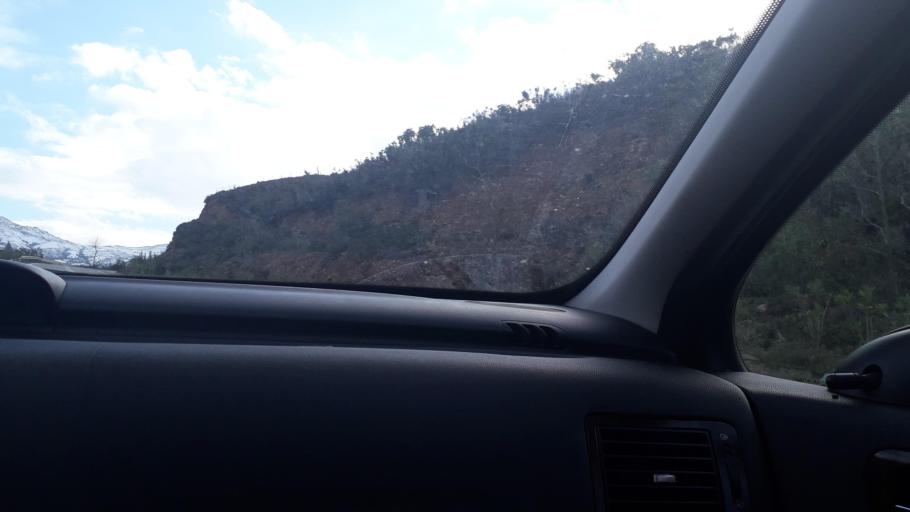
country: GR
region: Crete
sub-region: Nomos Rethymnis
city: Agia Foteini
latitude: 35.2781
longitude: 24.5620
